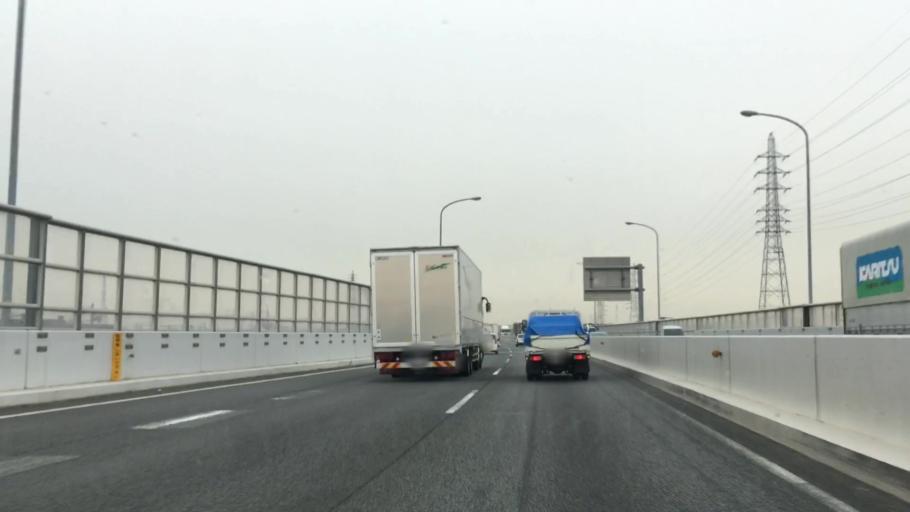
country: JP
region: Aichi
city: Chiryu
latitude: 34.9999
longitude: 137.0291
